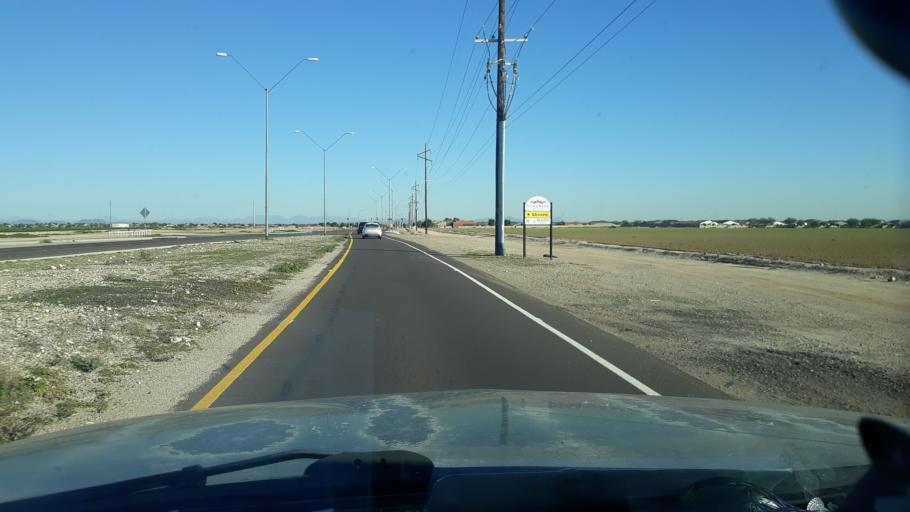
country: US
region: Arizona
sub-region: Maricopa County
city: Citrus Park
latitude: 33.5952
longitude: -112.4153
